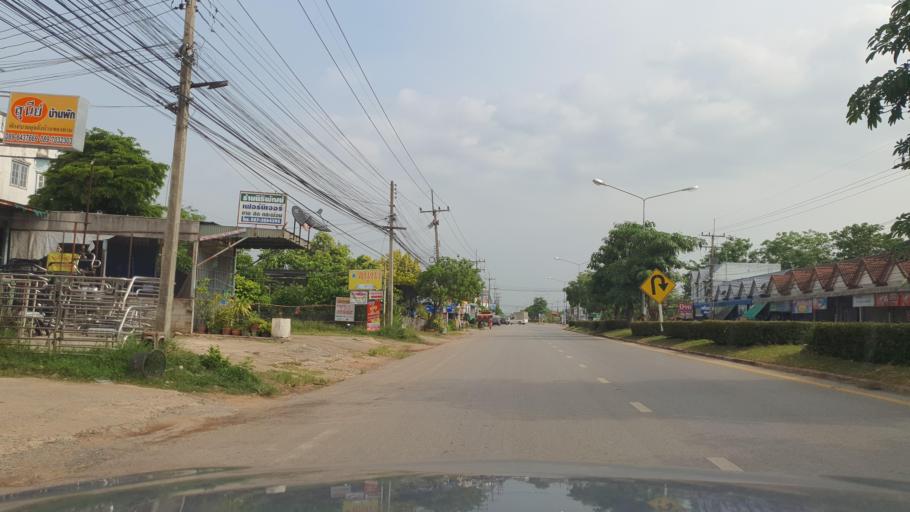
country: TH
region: Phitsanulok
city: Phitsanulok
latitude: 16.8580
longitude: 100.2524
